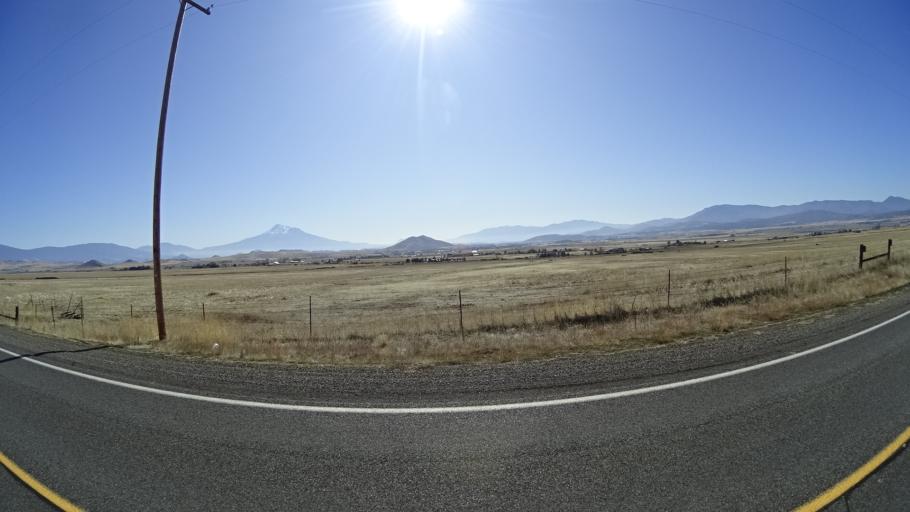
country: US
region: California
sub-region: Siskiyou County
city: Montague
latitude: 41.7712
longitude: -122.5379
